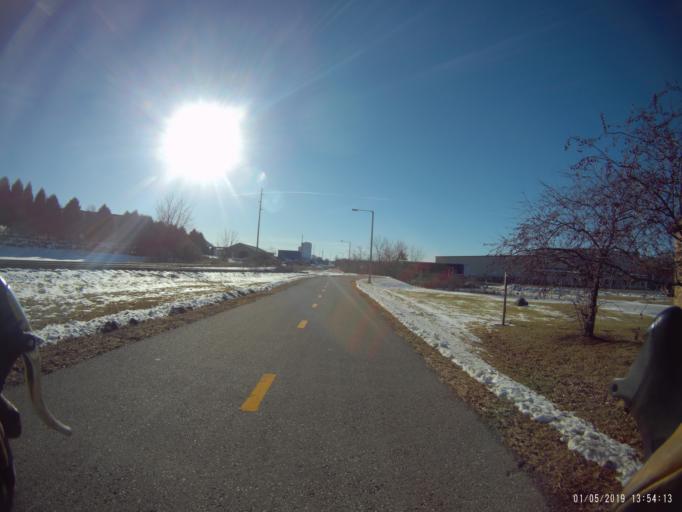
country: US
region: Wisconsin
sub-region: Dane County
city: Madison
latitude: 43.0416
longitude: -89.4046
